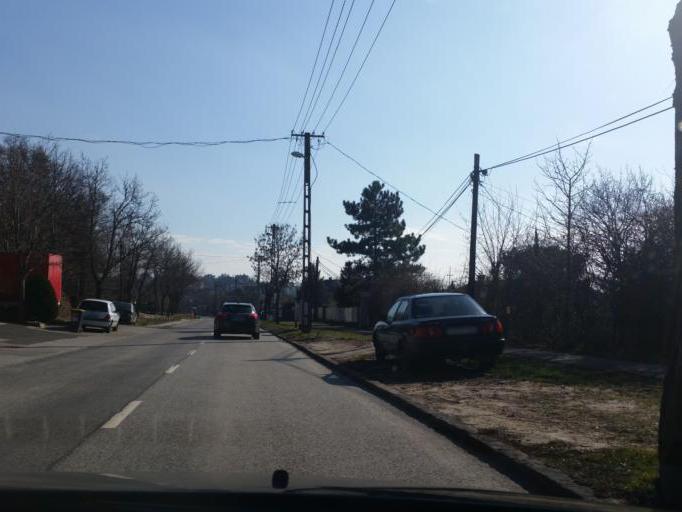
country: HU
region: Budapest
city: Budapest II. keruelet
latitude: 47.5320
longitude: 18.9960
